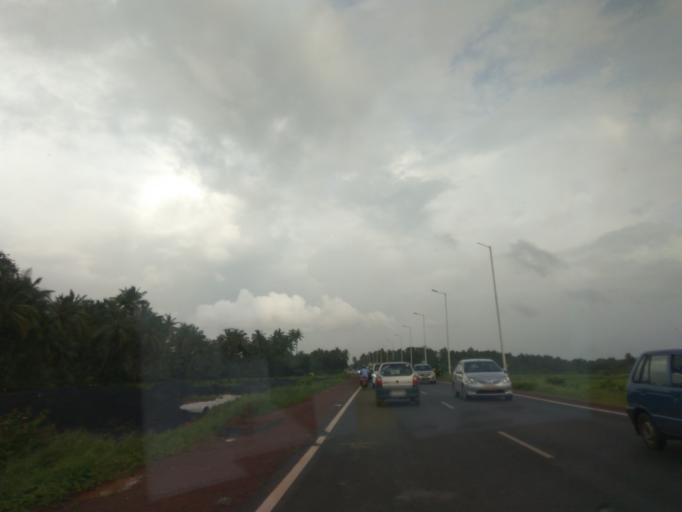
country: IN
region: Goa
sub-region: North Goa
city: Goa Velha
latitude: 15.4288
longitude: 73.8913
